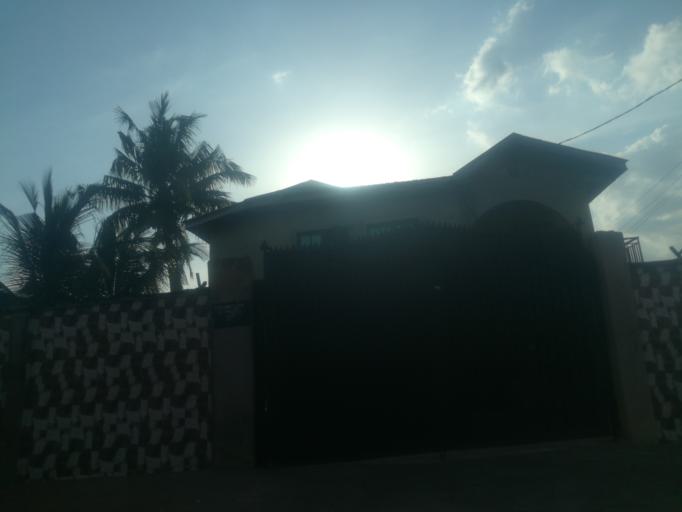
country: NG
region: Ogun
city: Abeokuta
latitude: 7.1172
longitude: 3.3265
